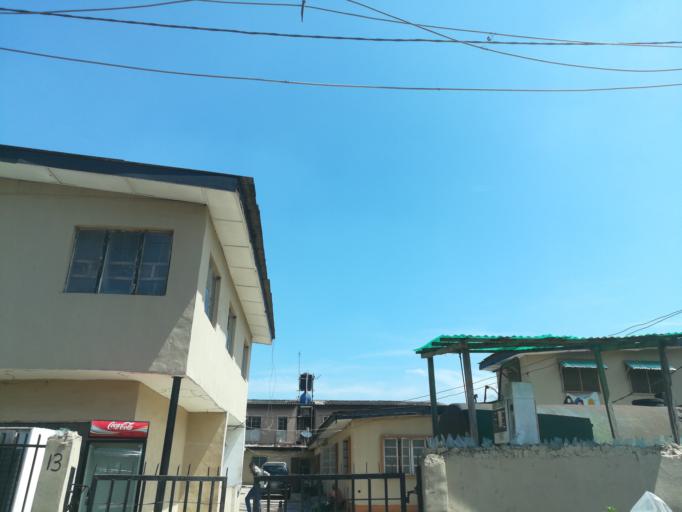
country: NG
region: Lagos
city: Oshodi
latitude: 6.5681
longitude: 3.3331
